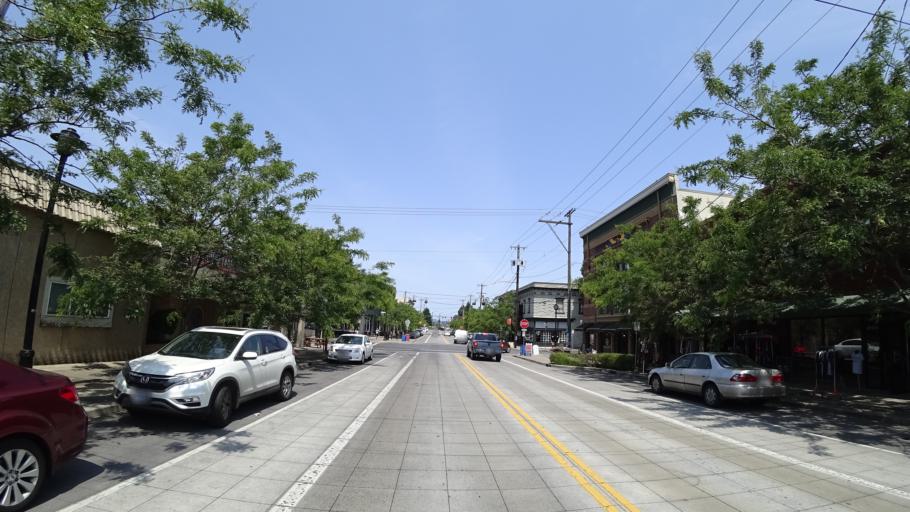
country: US
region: Oregon
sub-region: Multnomah County
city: Portland
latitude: 45.5821
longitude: -122.6870
